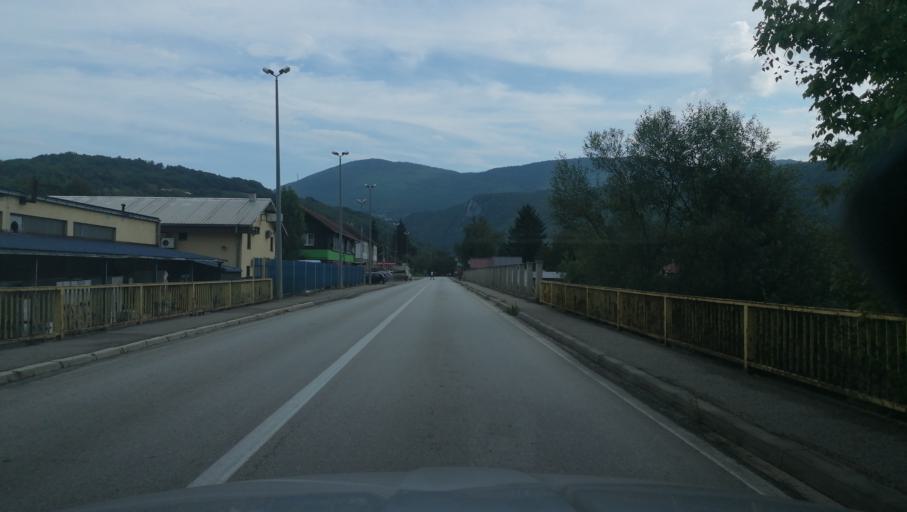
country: BA
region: Republika Srpska
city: Hiseti
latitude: 44.6159
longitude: 17.1436
